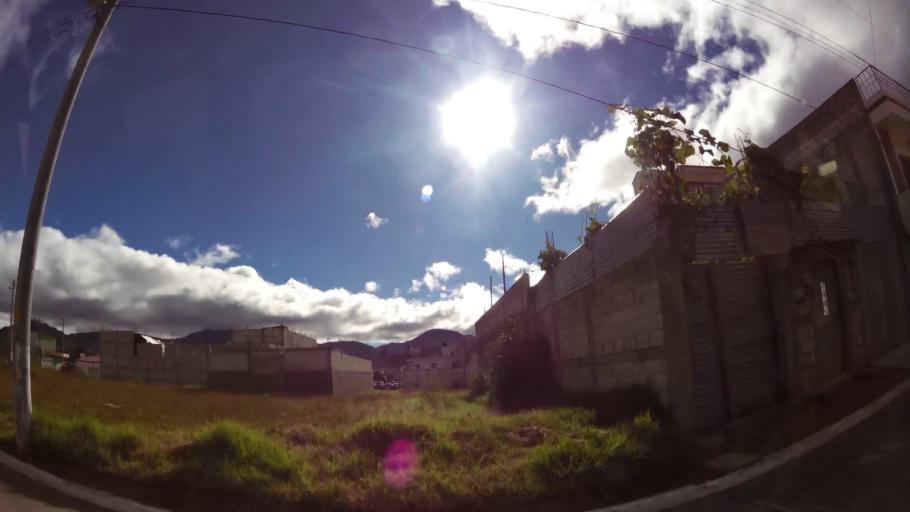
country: GT
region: Quetzaltenango
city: Salcaja
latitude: 14.8924
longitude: -91.4571
